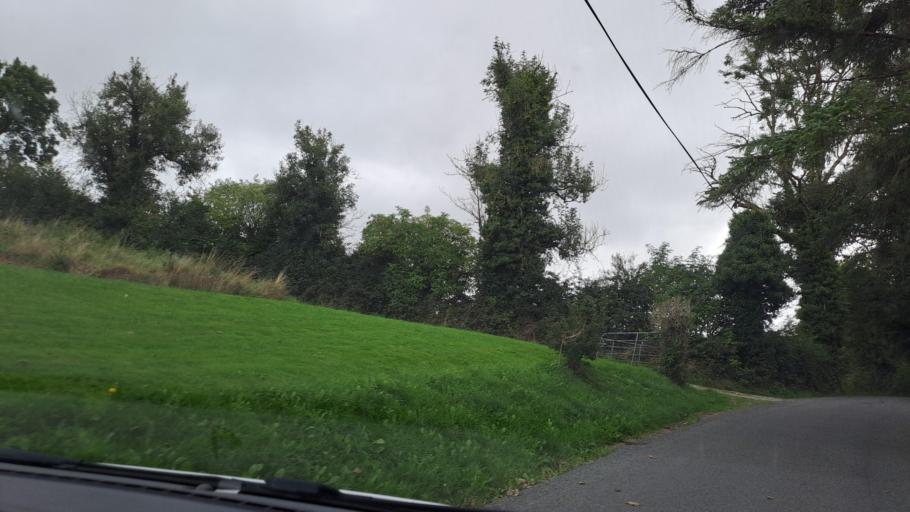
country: IE
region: Ulster
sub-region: County Monaghan
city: Carrickmacross
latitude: 54.0191
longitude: -6.7196
